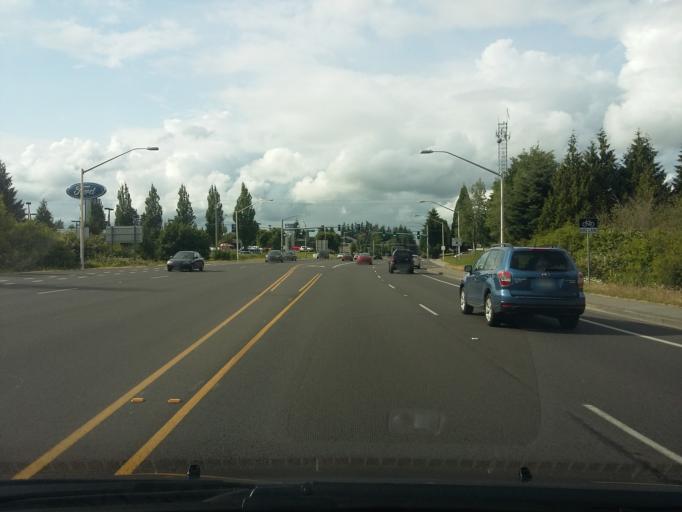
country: US
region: Washington
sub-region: Clark County
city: Walnut Grove
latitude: 45.6495
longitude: -122.6017
